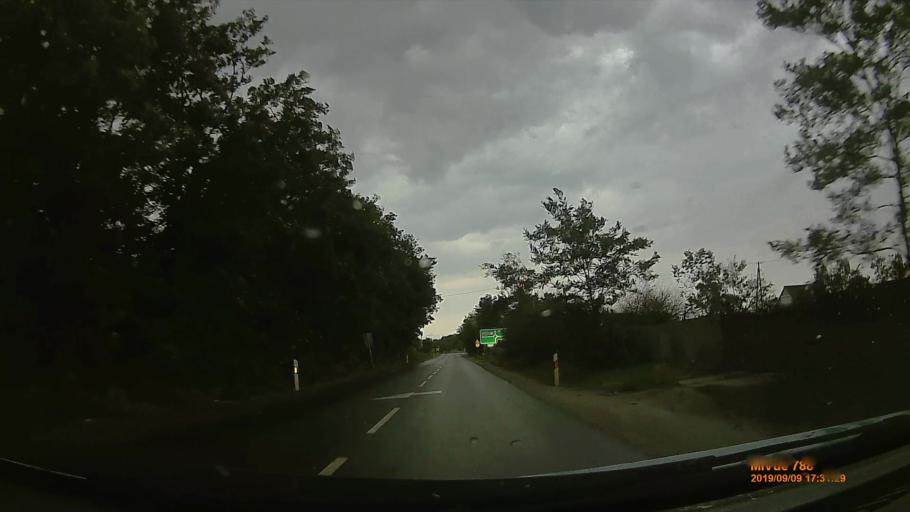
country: HU
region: Szabolcs-Szatmar-Bereg
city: Kalmanhaza
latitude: 47.9201
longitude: 21.6493
